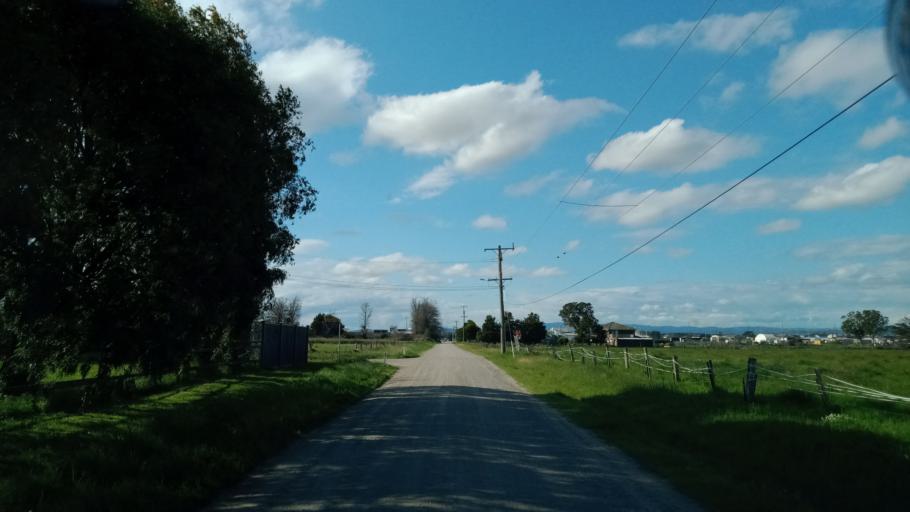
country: AU
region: Victoria
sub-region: Casey
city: Cranbourne West
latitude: -38.0836
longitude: 145.2502
